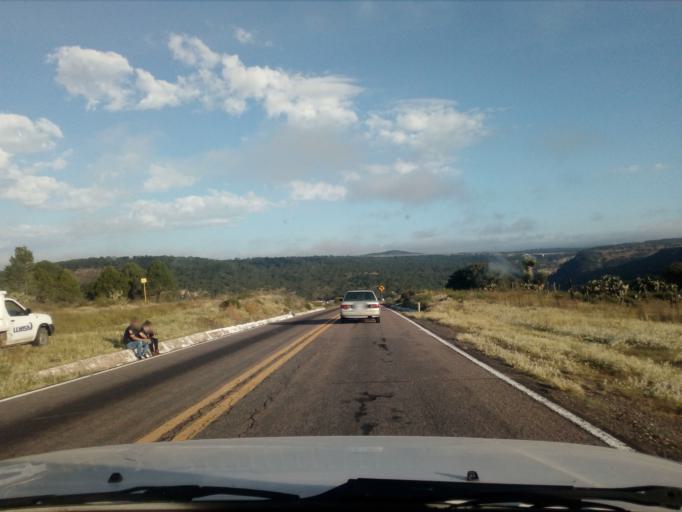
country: MX
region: Durango
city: Victoria de Durango
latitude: 23.9550
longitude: -104.8496
